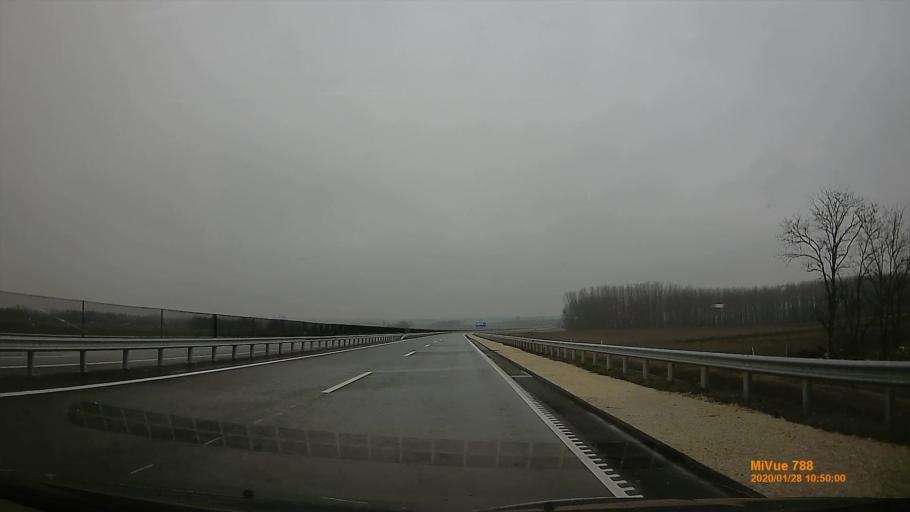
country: HU
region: Pest
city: Monor
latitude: 47.3771
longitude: 19.4365
